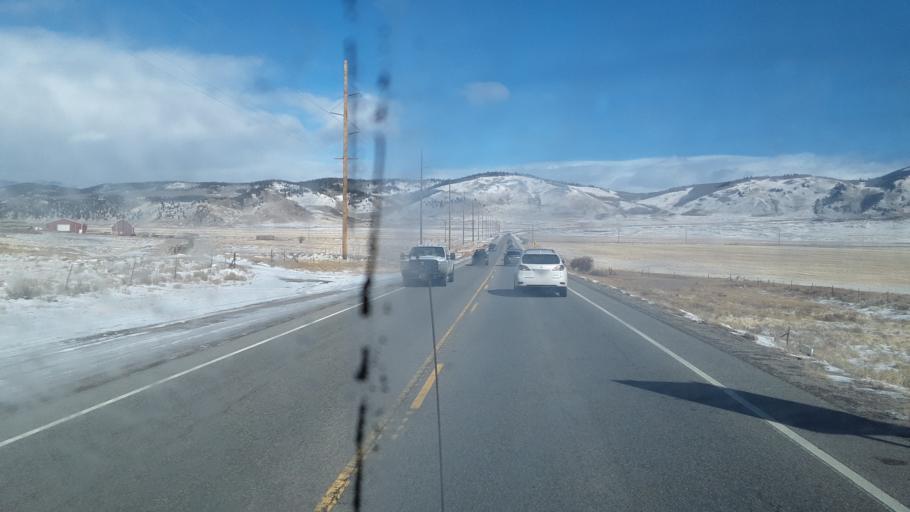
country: US
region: Colorado
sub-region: Summit County
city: Breckenridge
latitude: 39.3877
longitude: -105.7892
